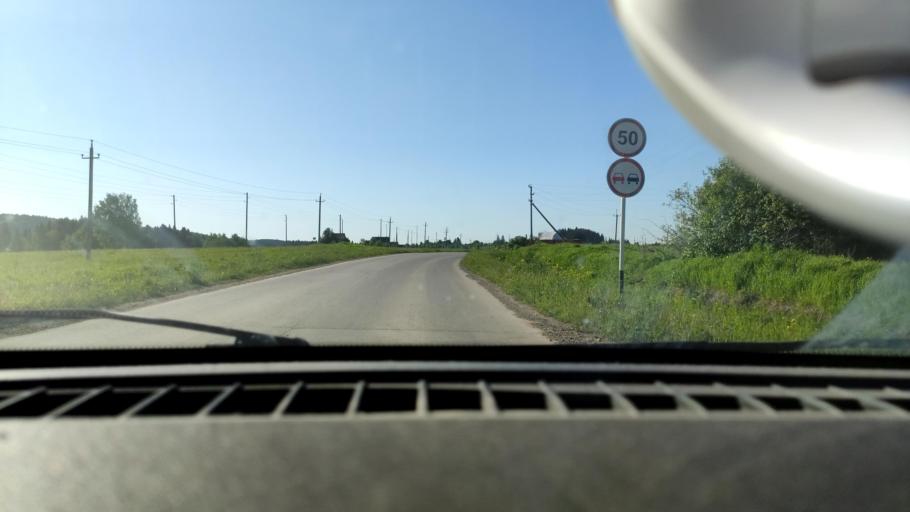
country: RU
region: Perm
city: Novyye Lyady
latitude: 58.1802
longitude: 56.5548
